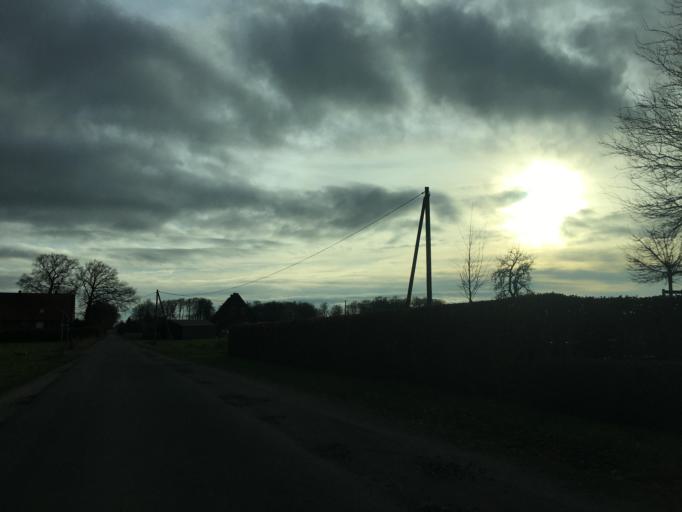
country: DE
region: North Rhine-Westphalia
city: Ludinghausen
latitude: 51.7789
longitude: 7.3803
